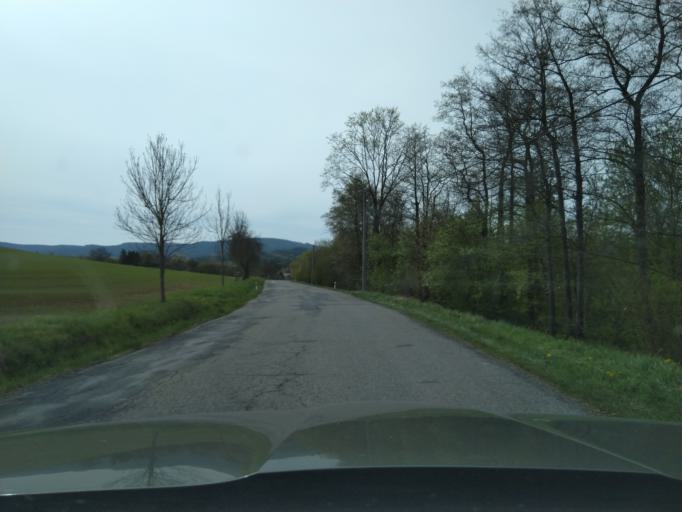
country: CZ
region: Plzensky
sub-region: Okres Klatovy
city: Kasperske Hory
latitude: 49.2108
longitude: 13.6128
